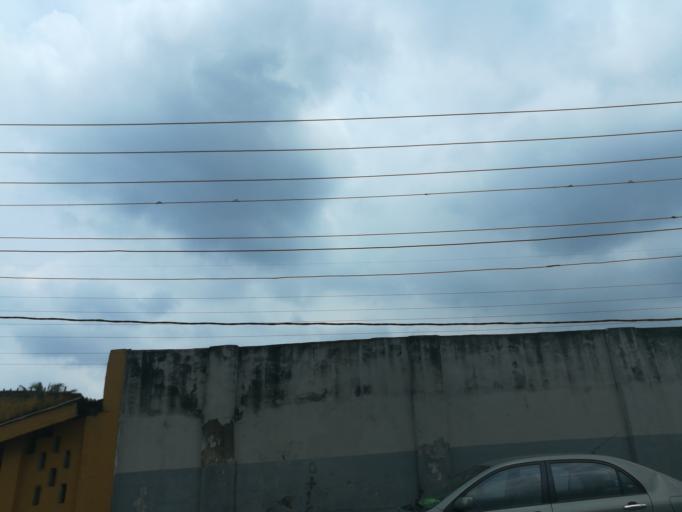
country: NG
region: Lagos
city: Agege
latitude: 6.6205
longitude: 3.3454
